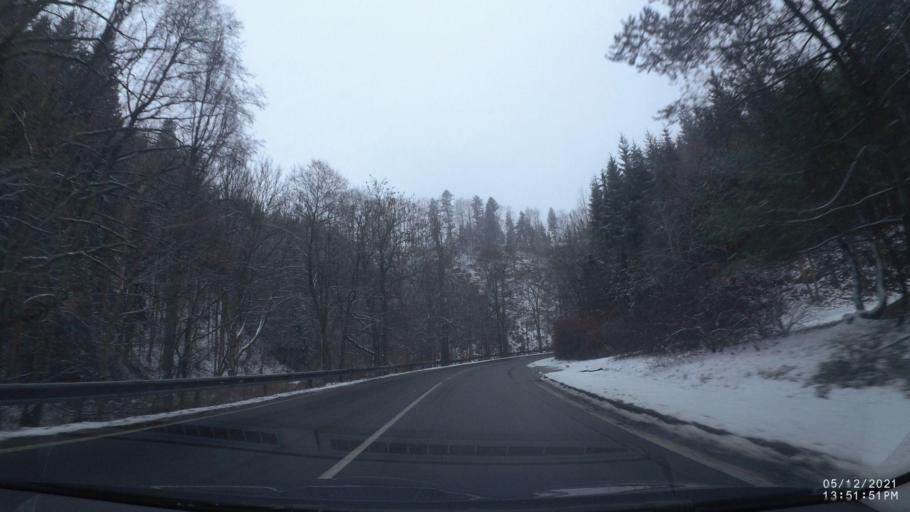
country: CZ
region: Kralovehradecky
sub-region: Okres Nachod
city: Police nad Metuji
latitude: 50.5251
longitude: 16.2228
